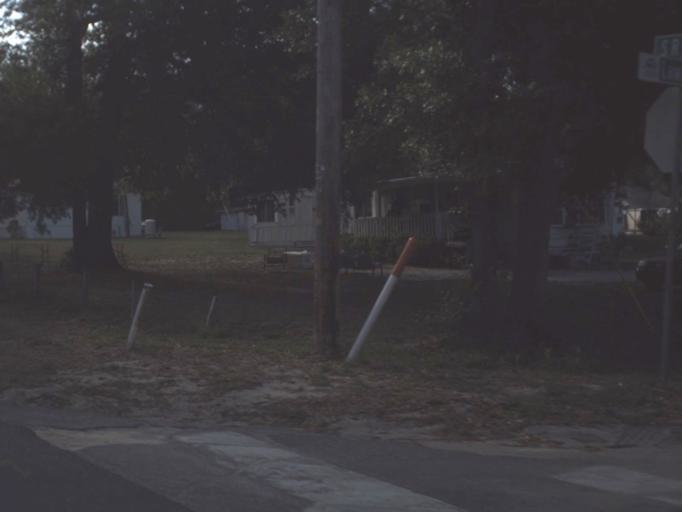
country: US
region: Florida
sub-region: Lake County
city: Mount Plymouth
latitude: 28.8078
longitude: -81.5662
